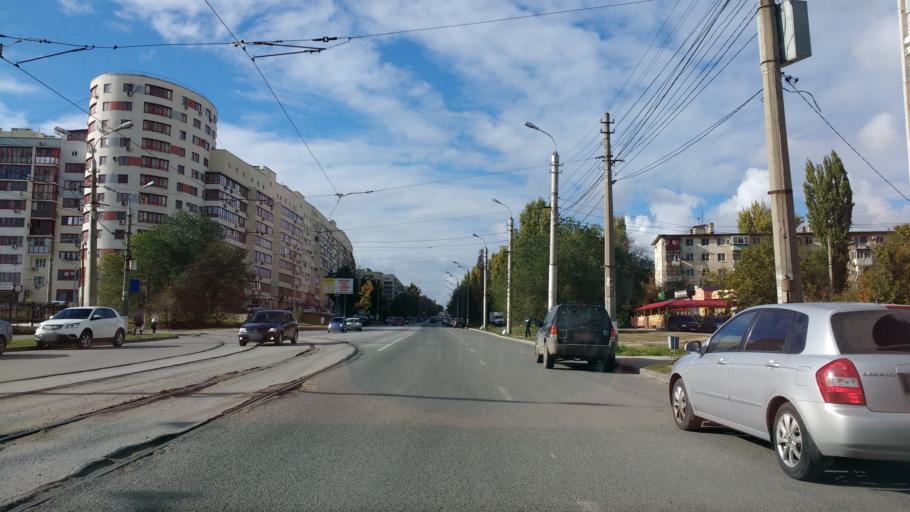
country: RU
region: Volgograd
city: Krasnoslobodsk
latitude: 48.7717
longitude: 44.5648
